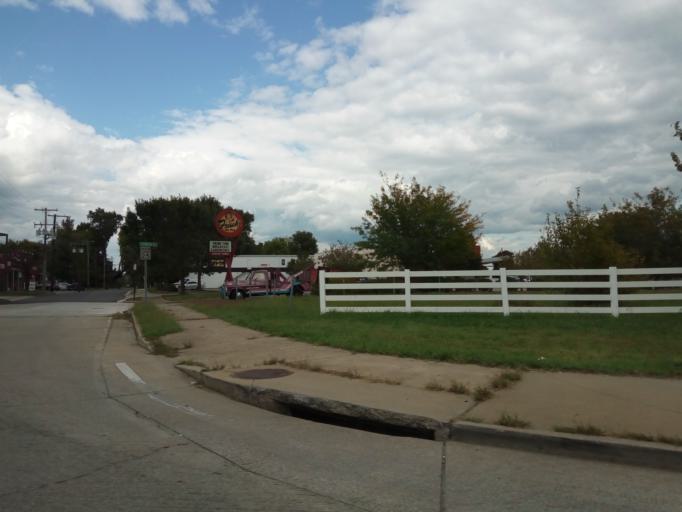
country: US
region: Kentucky
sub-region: Jefferson County
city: Audubon Park
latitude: 38.1969
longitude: -85.7078
